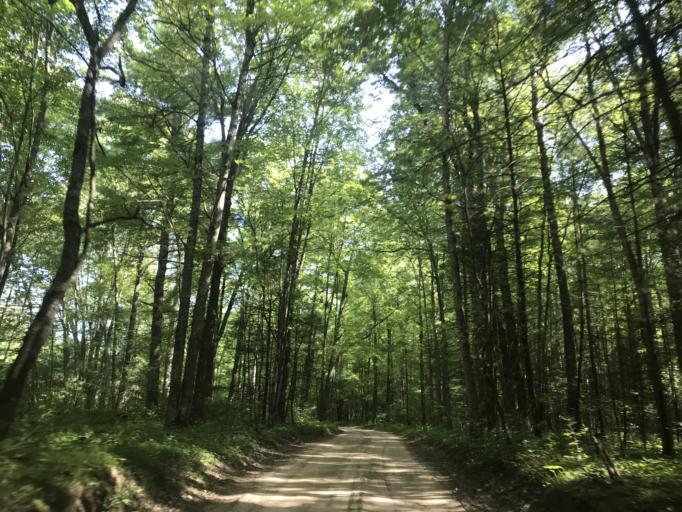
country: US
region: Michigan
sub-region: Newaygo County
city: Newaygo
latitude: 43.4600
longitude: -85.7629
